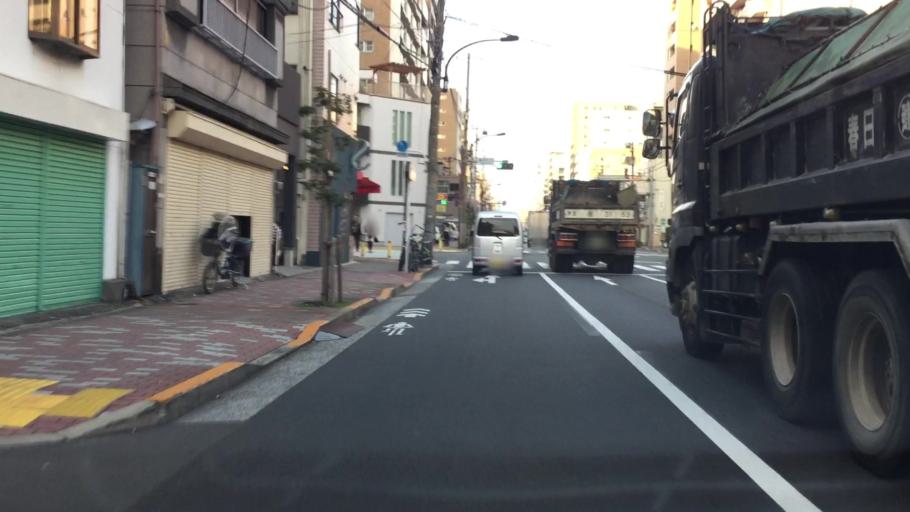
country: JP
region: Tokyo
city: Urayasu
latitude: 35.6970
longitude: 139.8053
